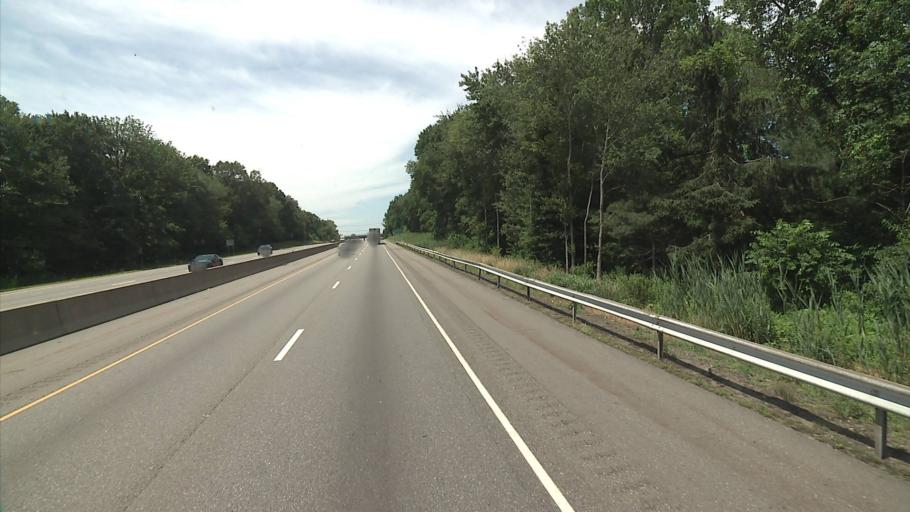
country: US
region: Connecticut
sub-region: Middlesex County
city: Clinton
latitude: 41.2893
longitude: -72.5081
